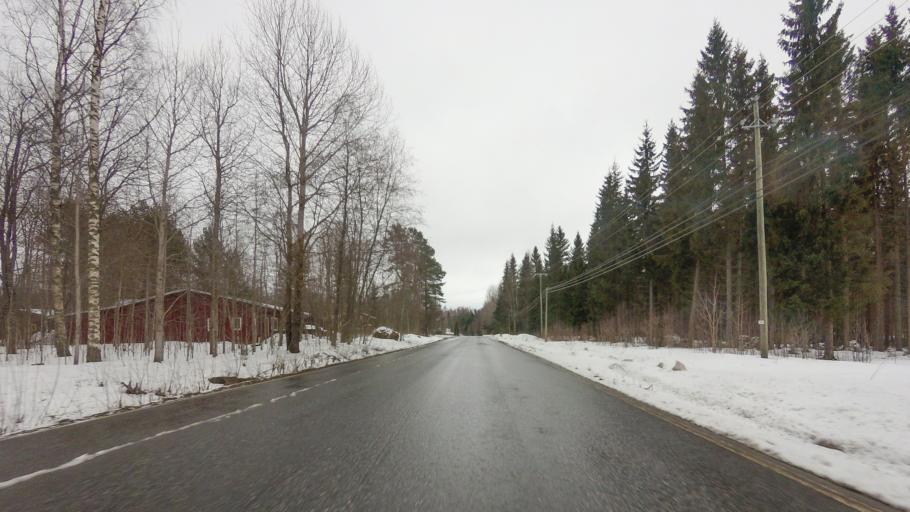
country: FI
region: Southern Savonia
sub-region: Savonlinna
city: Savonlinna
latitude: 61.9366
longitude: 28.8717
